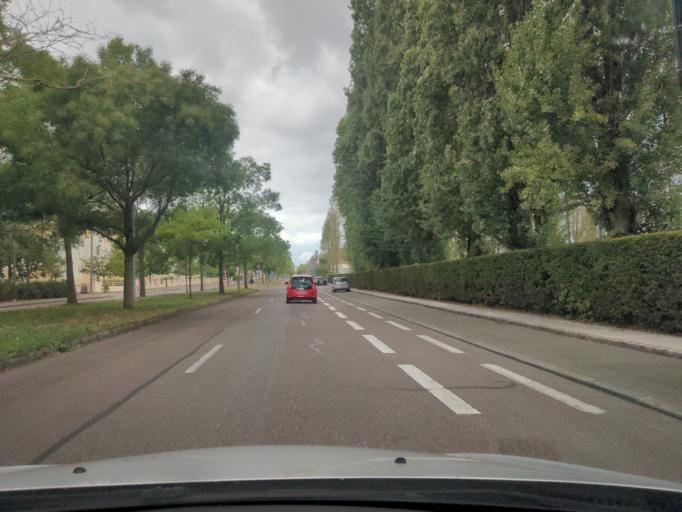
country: FR
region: Bourgogne
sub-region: Departement de la Cote-d'Or
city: Saint-Apollinaire
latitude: 47.3379
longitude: 5.0551
